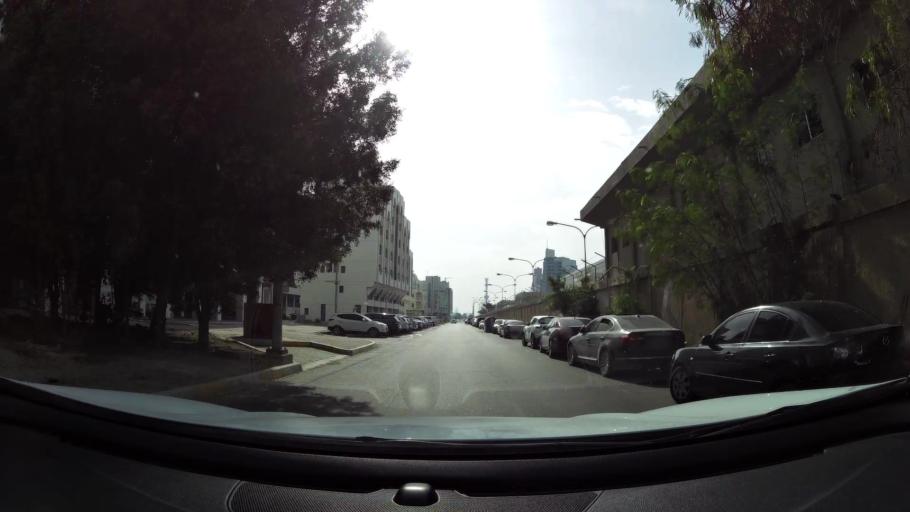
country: AE
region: Abu Dhabi
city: Abu Dhabi
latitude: 24.4574
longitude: 54.3894
